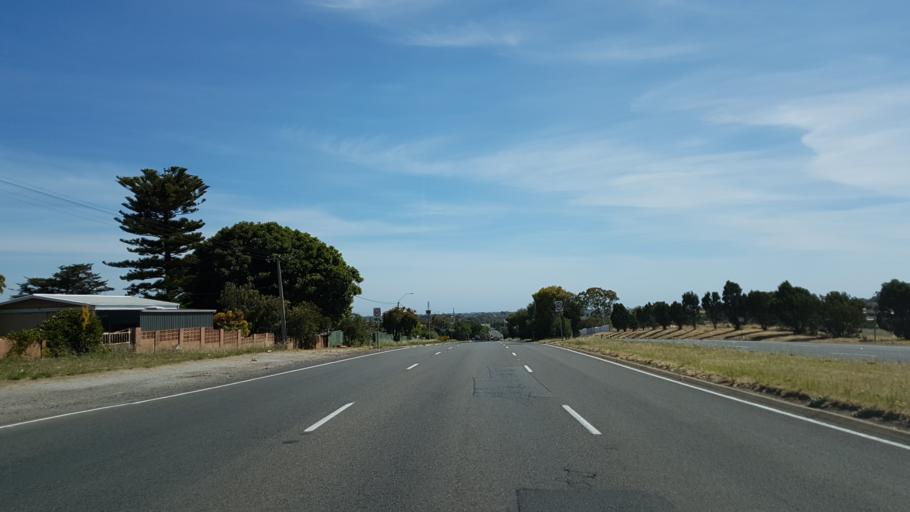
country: AU
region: South Australia
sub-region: Marion
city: Trott Park
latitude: -35.0715
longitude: 138.5537
